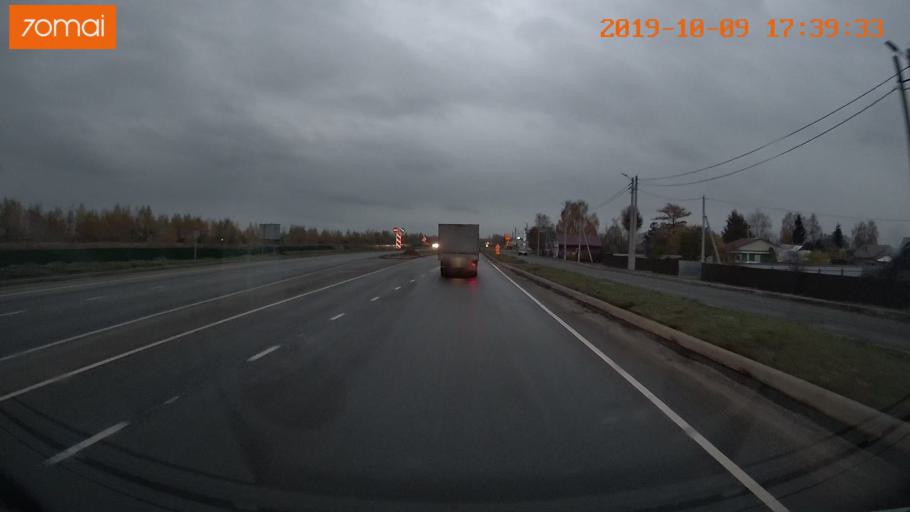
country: RU
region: Ivanovo
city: Bogorodskoye
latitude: 57.0597
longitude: 40.9597
